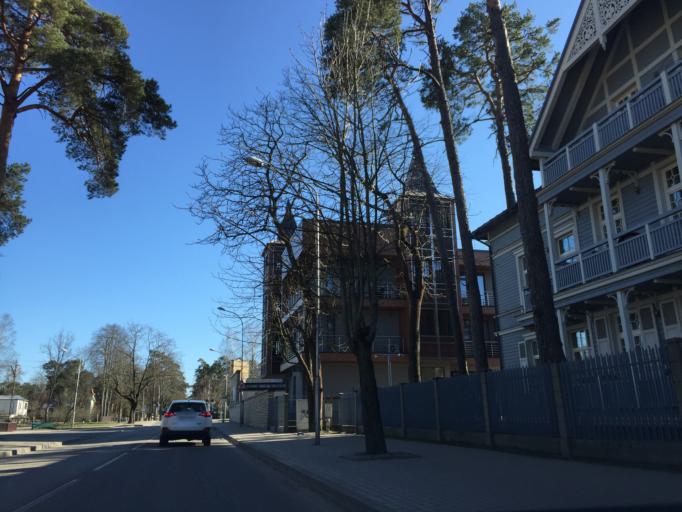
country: LV
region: Babite
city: Pinki
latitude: 56.9831
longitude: 23.8561
